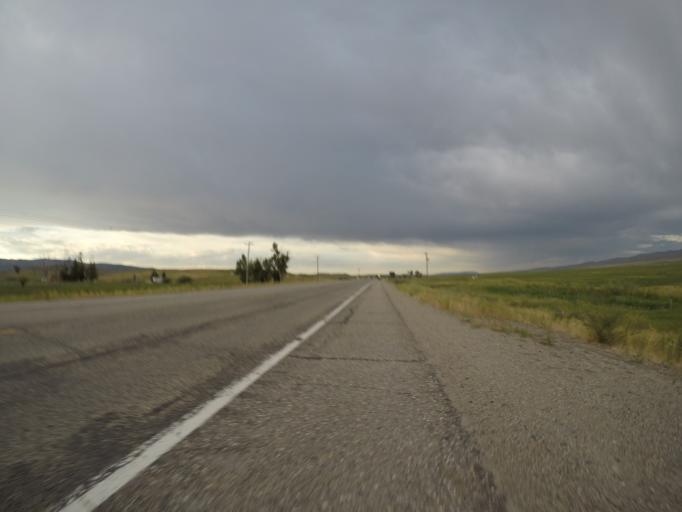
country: US
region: Utah
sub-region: Rich County
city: Randolph
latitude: 42.0393
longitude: -110.9316
